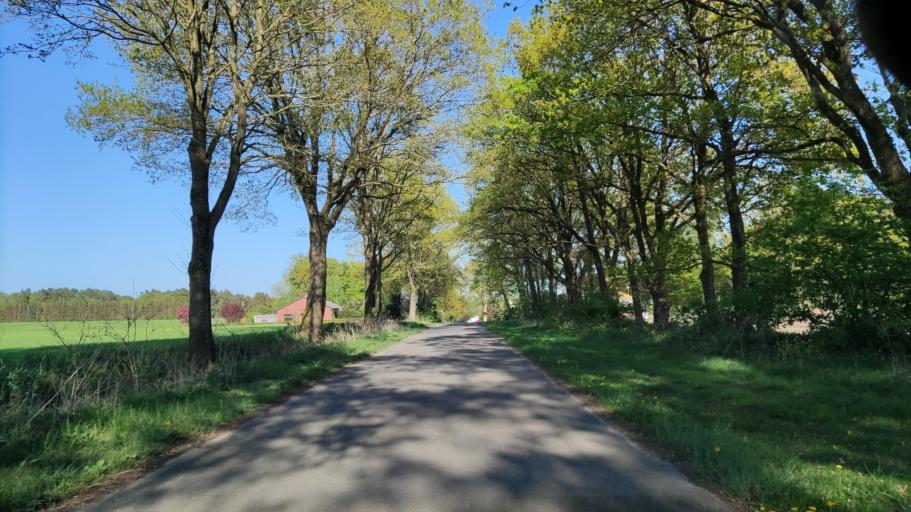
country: DE
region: Lower Saxony
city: Soderstorf
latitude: 53.1605
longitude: 10.1440
